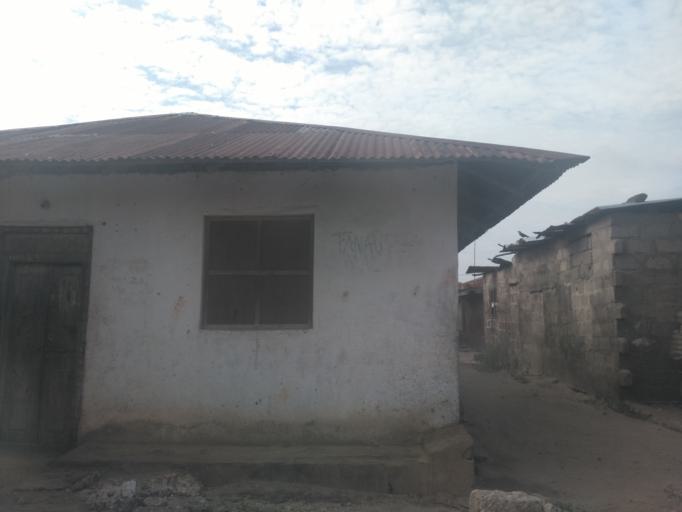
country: TZ
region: Zanzibar Urban/West
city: Zanzibar
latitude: -6.1556
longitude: 39.2102
